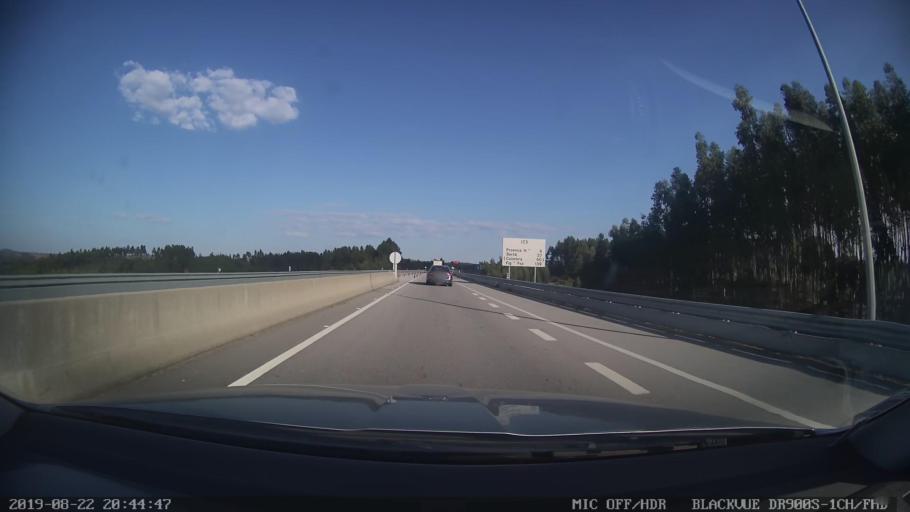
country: PT
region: Castelo Branco
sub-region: Proenca-A-Nova
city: Proenca-a-Nova
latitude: 39.7101
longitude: -7.8577
